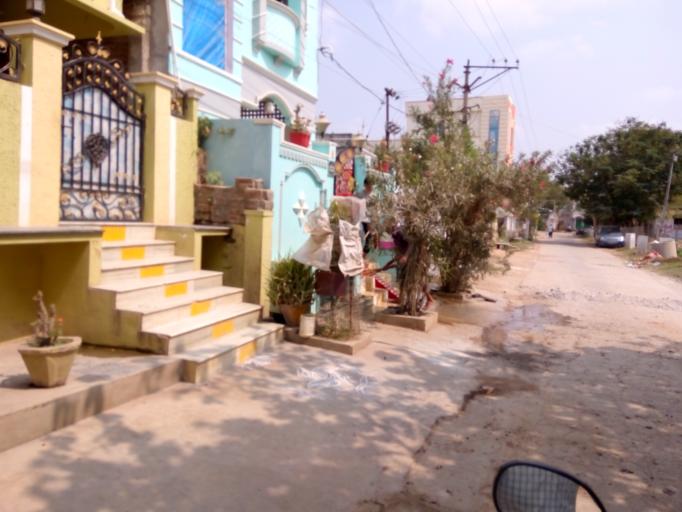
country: IN
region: Andhra Pradesh
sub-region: Prakasam
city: pedda nakkalapalem
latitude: 15.9692
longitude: 80.2753
